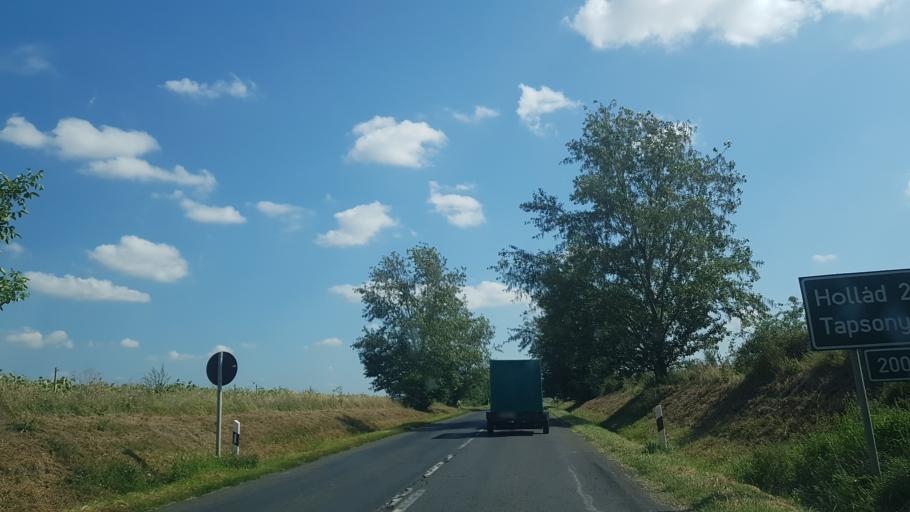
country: HU
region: Somogy
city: Bohonye
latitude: 46.4508
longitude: 17.3727
